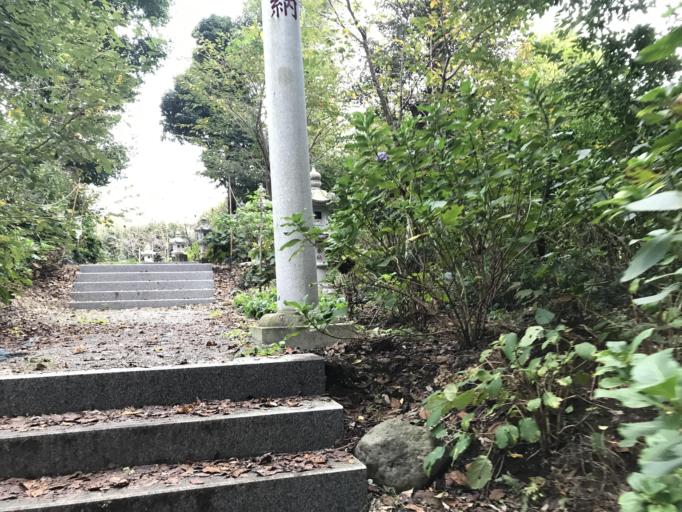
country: JP
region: Saitama
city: Shiraoka
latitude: 36.0041
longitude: 139.6571
